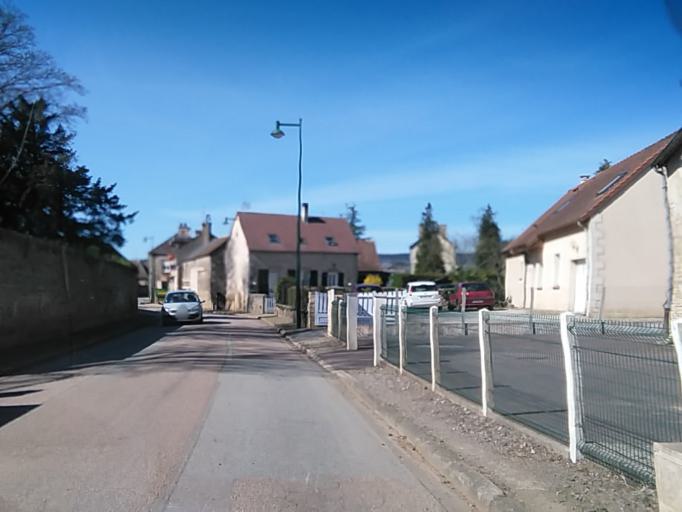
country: FR
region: Lower Normandy
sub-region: Departement de l'Orne
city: Conde-sur-Sarthe
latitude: 48.4693
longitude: 0.0172
